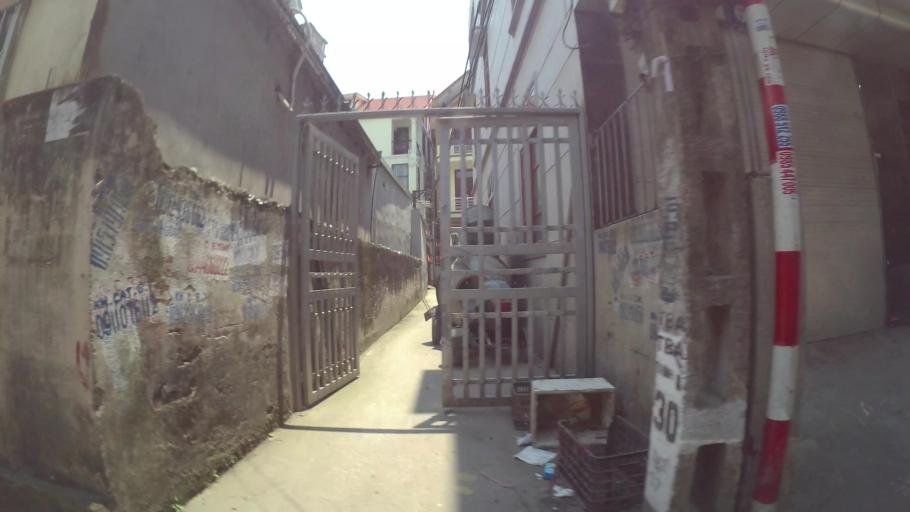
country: VN
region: Ha Noi
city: Hoan Kiem
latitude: 21.0268
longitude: 105.8862
